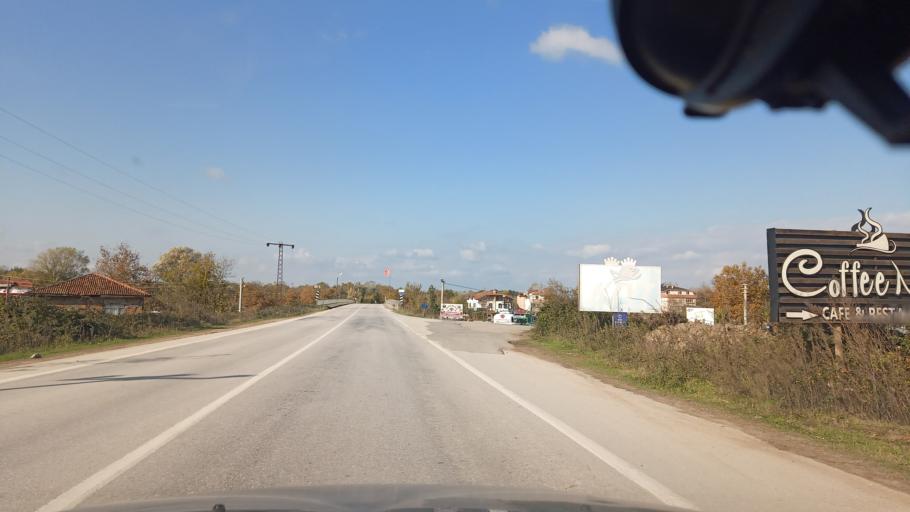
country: TR
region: Sakarya
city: Karasu
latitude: 41.1183
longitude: 30.6477
